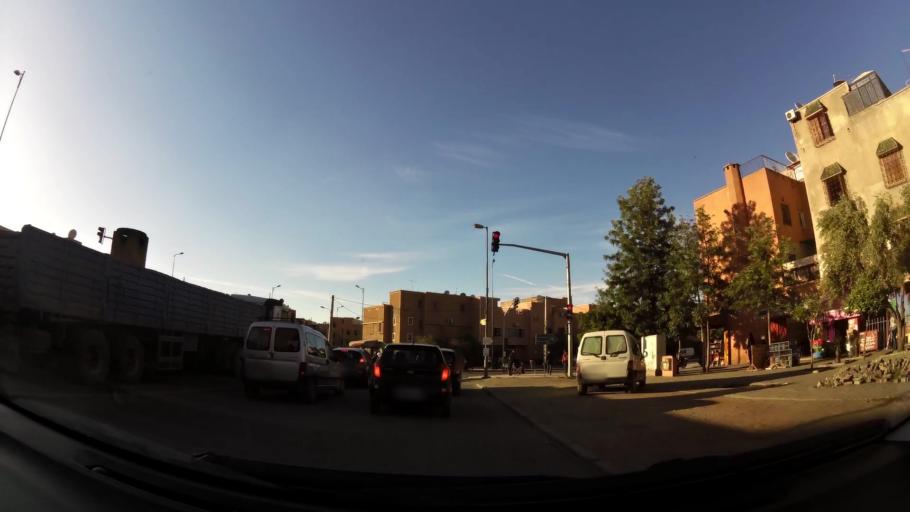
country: MA
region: Marrakech-Tensift-Al Haouz
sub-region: Marrakech
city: Marrakesh
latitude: 31.6202
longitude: -8.0584
